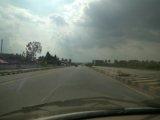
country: IN
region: Karnataka
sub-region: Kolar
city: Kolar
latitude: 13.1287
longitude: 77.9939
